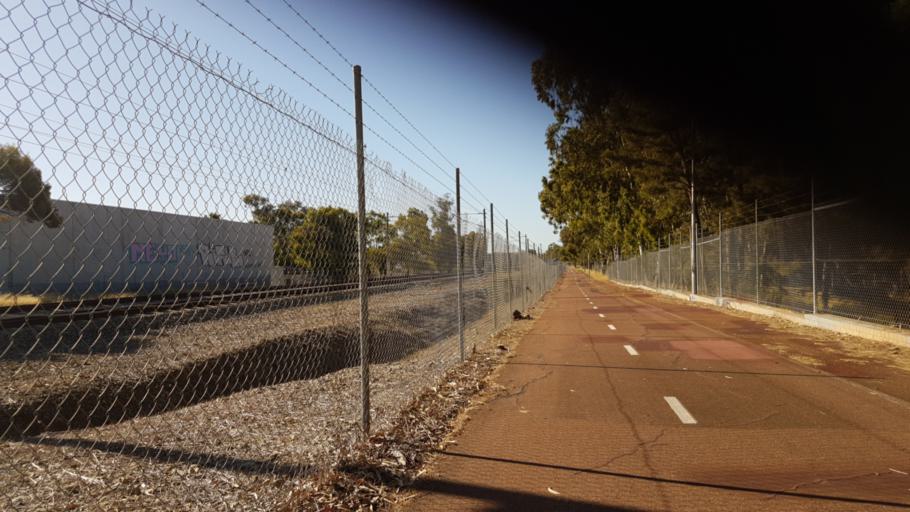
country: AU
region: Western Australia
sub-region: Gosnells
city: Maddington
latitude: -32.0428
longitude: 115.9753
